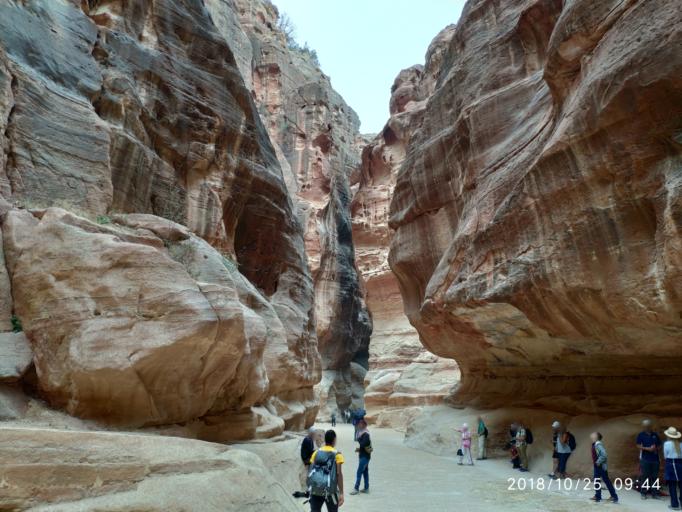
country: JO
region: Ma'an
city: Petra
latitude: 30.3230
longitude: 35.4530
